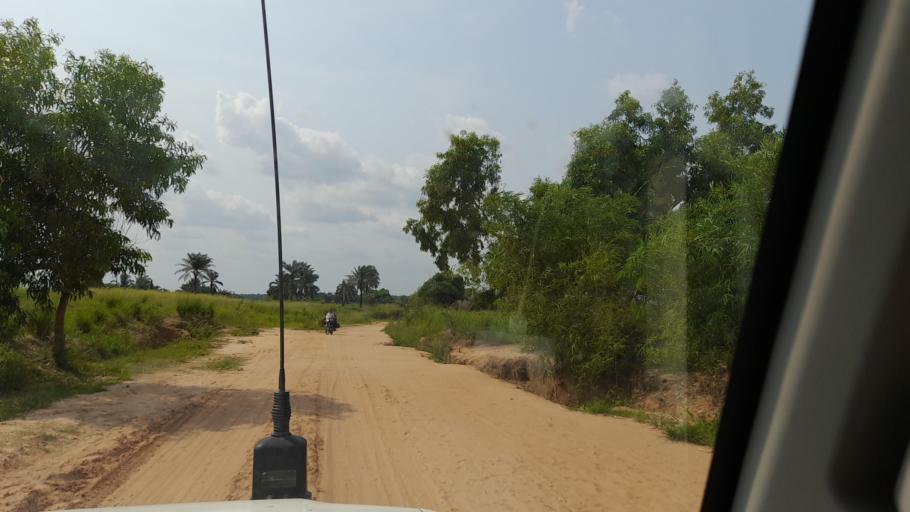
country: CD
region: Kasai-Occidental
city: Kananga
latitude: -5.9141
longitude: 22.4778
